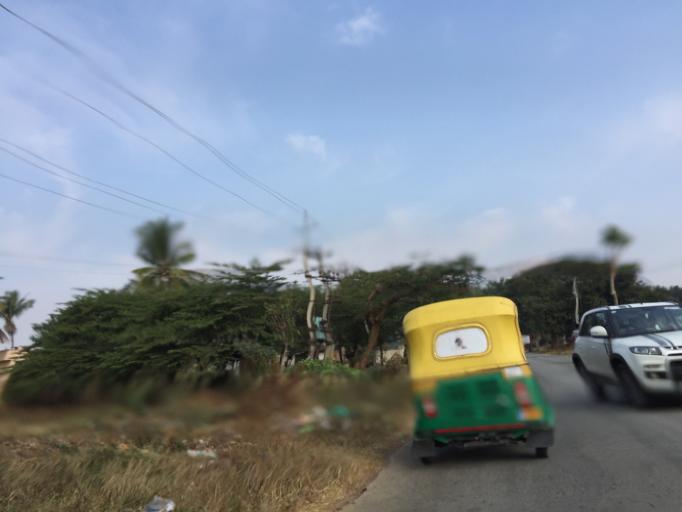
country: IN
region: Karnataka
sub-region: Bangalore Rural
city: Devanhalli
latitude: 13.3384
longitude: 77.6890
